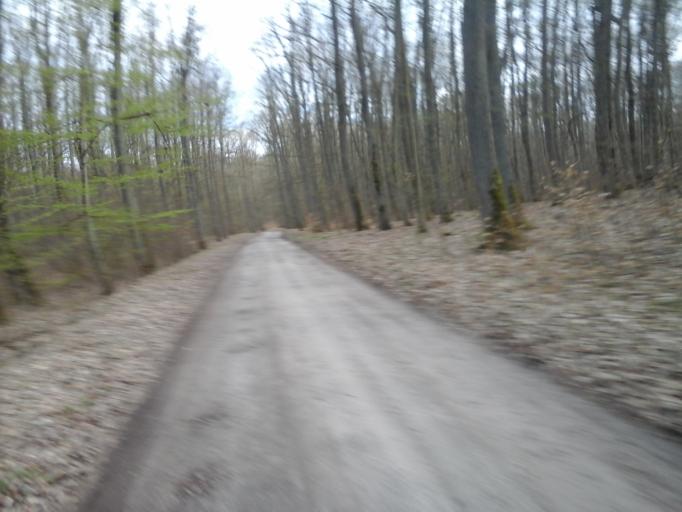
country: PL
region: West Pomeranian Voivodeship
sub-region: Powiat choszczenski
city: Bierzwnik
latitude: 53.0488
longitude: 15.5952
